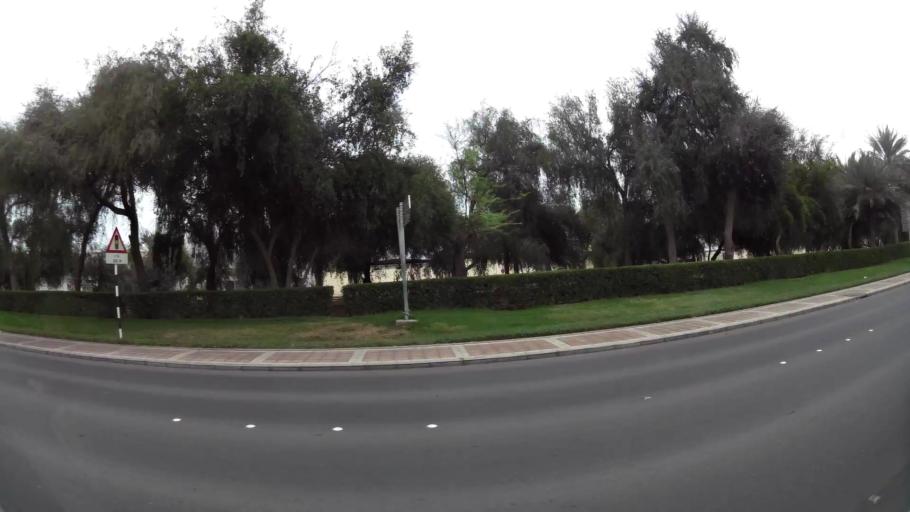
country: AE
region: Abu Dhabi
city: Abu Dhabi
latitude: 24.4318
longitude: 54.4161
